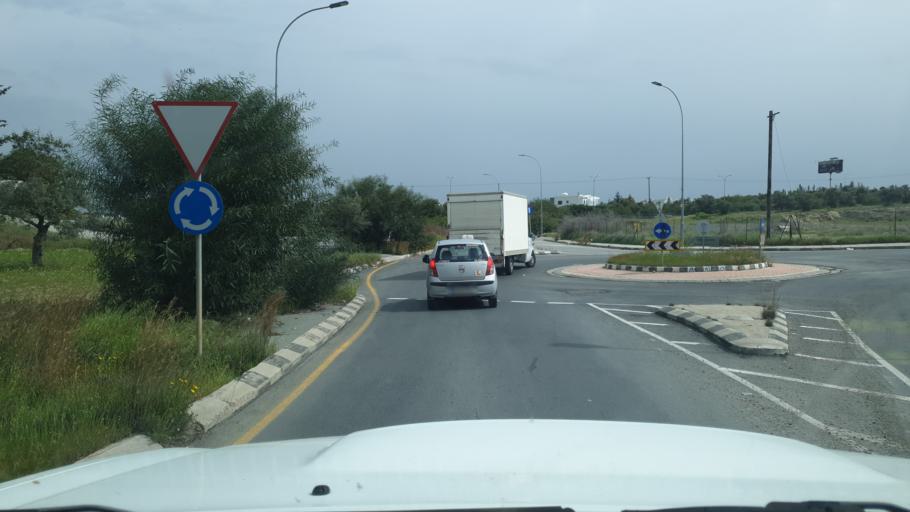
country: CY
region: Lefkosia
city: Geri
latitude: 35.1048
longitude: 33.3666
